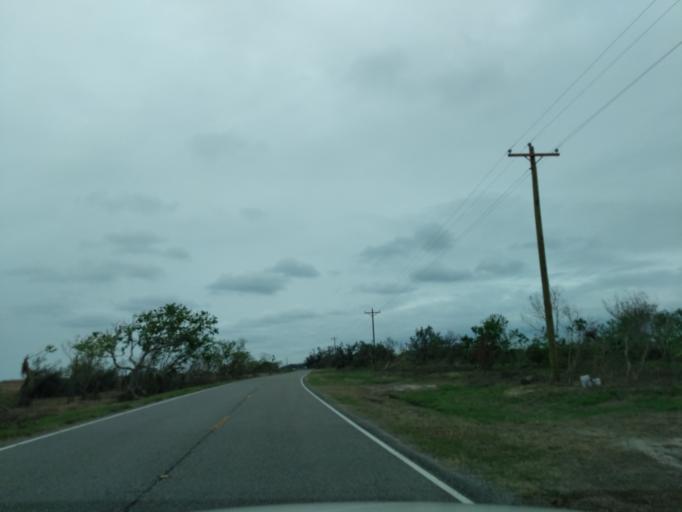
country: US
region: Louisiana
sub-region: Cameron Parish
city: Cameron
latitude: 29.7862
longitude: -93.1737
